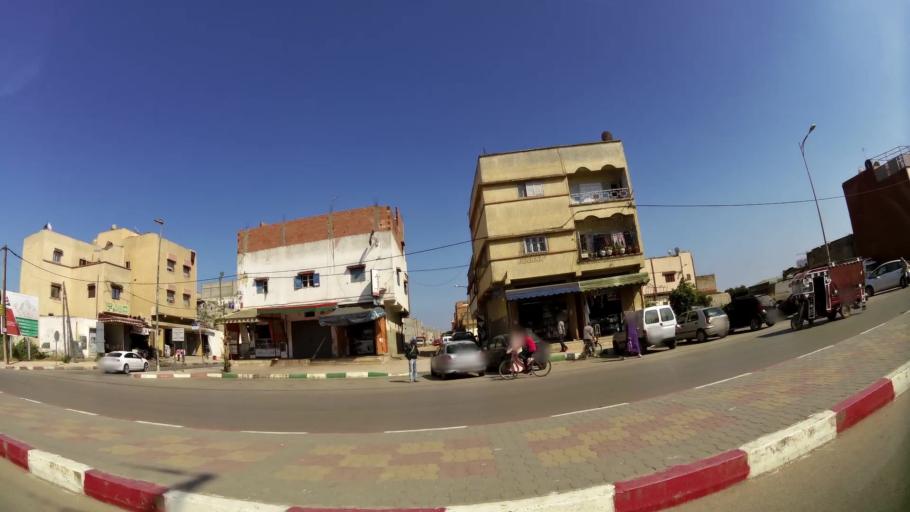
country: MA
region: Rabat-Sale-Zemmour-Zaer
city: Sale
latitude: 34.0686
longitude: -6.7607
